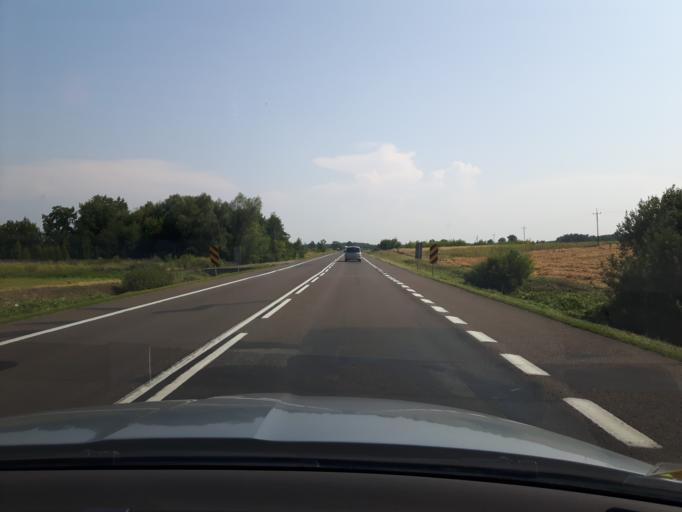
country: PL
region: Masovian Voivodeship
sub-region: Powiat ciechanowski
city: Glinojeck
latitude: 52.7993
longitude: 20.2698
